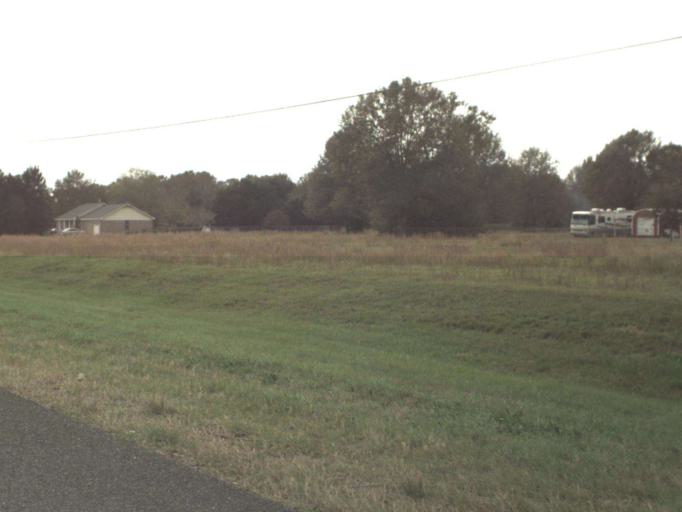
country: US
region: Florida
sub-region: Escambia County
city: Cantonment
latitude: 30.6657
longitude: -87.3515
